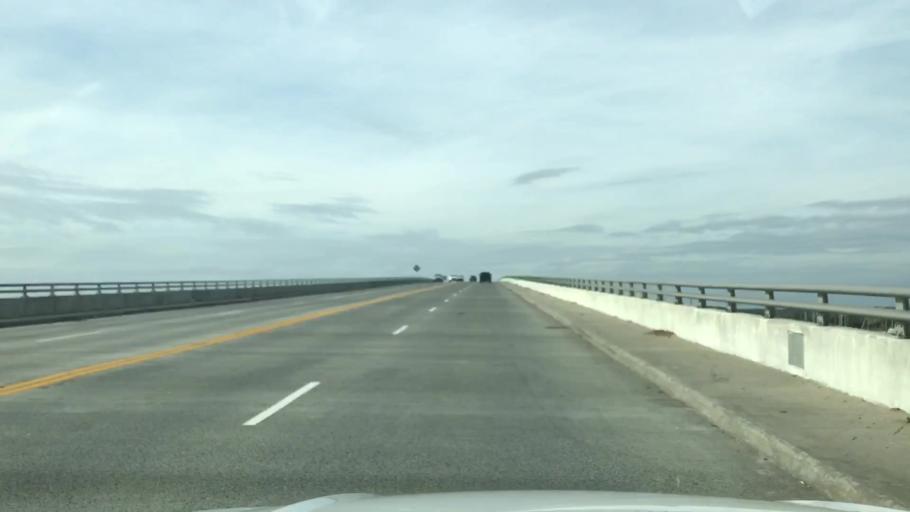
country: US
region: South Carolina
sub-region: Charleston County
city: Charleston
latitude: 32.7531
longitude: -80.0066
